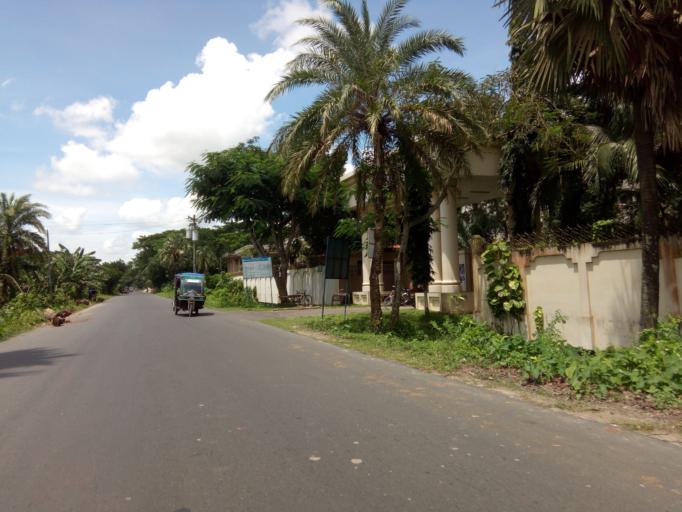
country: BD
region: Dhaka
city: Tungipara
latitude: 22.9033
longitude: 89.8838
